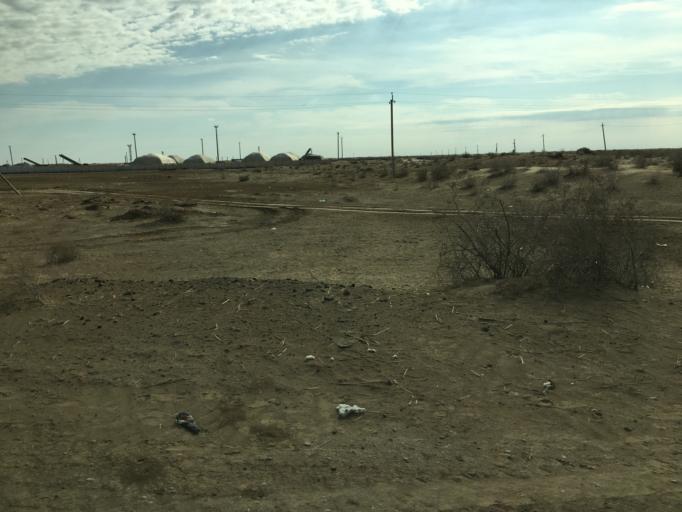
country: TM
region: Ahal
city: Tejen
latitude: 37.4463
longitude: 61.1295
